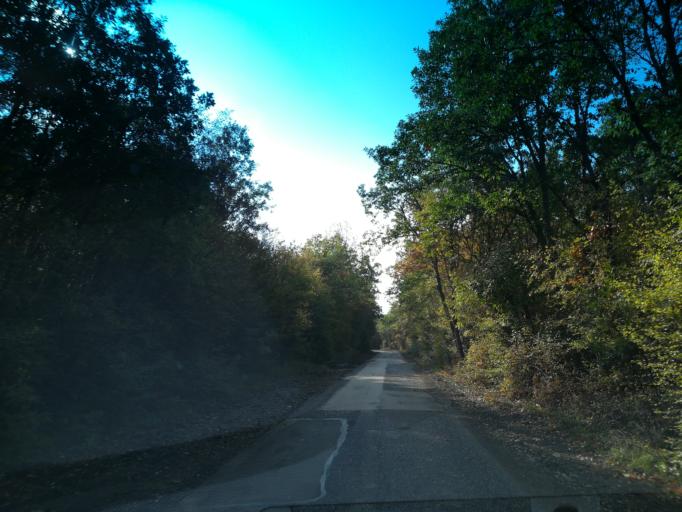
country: BG
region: Stara Zagora
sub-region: Obshtina Nikolaevo
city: Elkhovo
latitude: 42.3250
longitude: 25.3987
